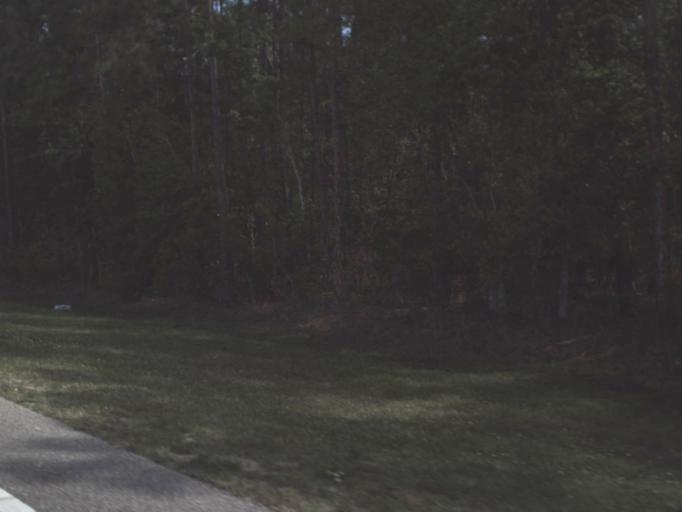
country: US
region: Florida
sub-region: Flagler County
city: Bunnell
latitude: 29.4990
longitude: -81.2647
